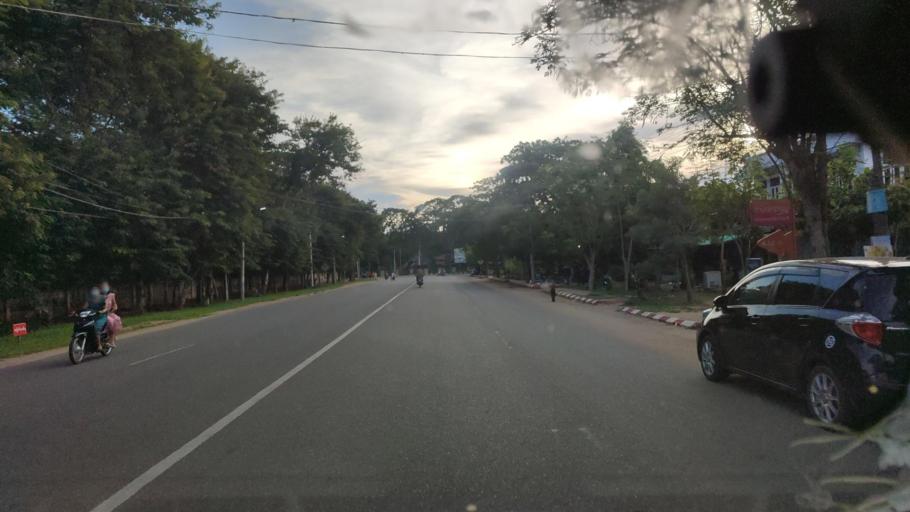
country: MM
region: Magway
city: Magway
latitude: 20.1395
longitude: 94.9326
